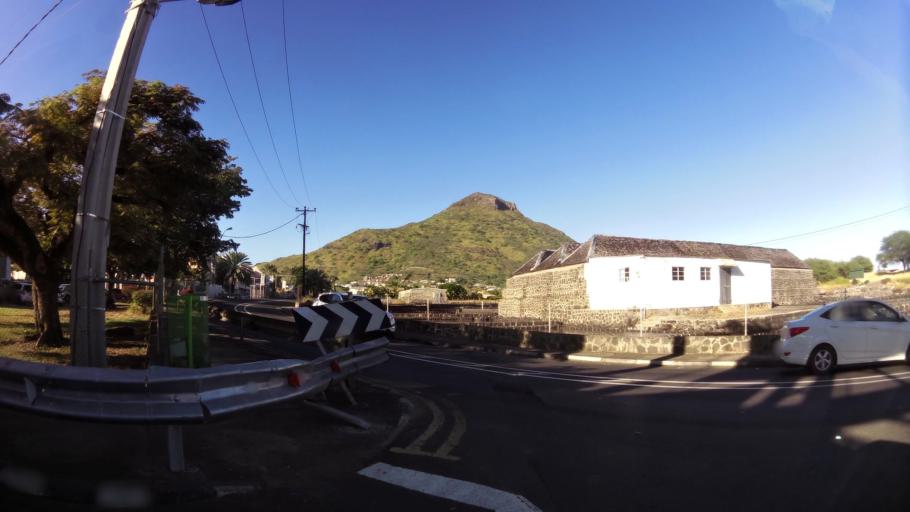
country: MU
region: Black River
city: Tamarin
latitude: -20.3292
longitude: 57.3779
